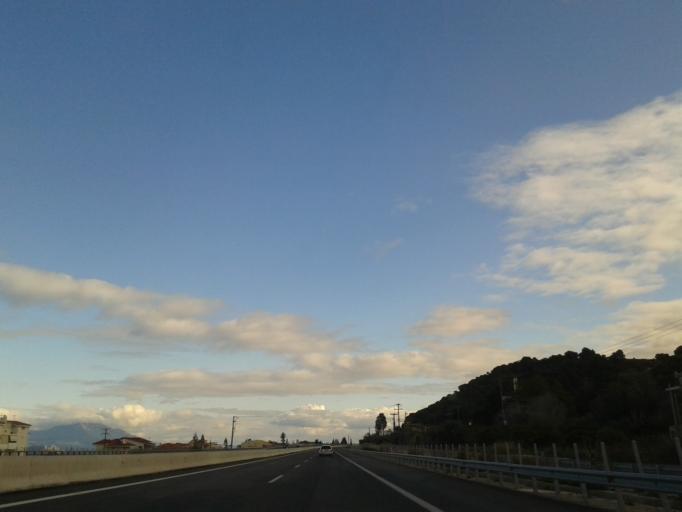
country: GR
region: Peloponnese
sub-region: Nomos Korinthias
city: Kato Dhiminio
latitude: 38.0425
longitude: 22.7021
